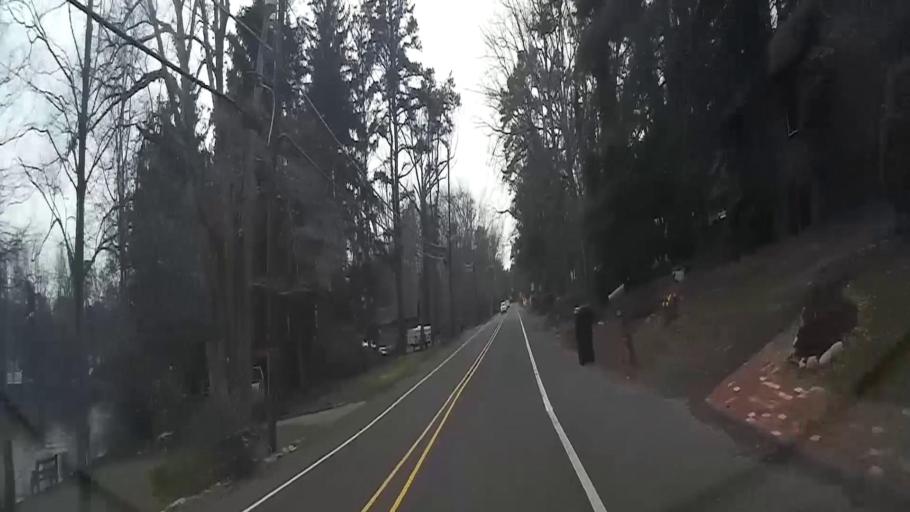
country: US
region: New Jersey
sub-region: Burlington County
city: Medford Lakes
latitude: 39.8663
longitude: -74.8489
